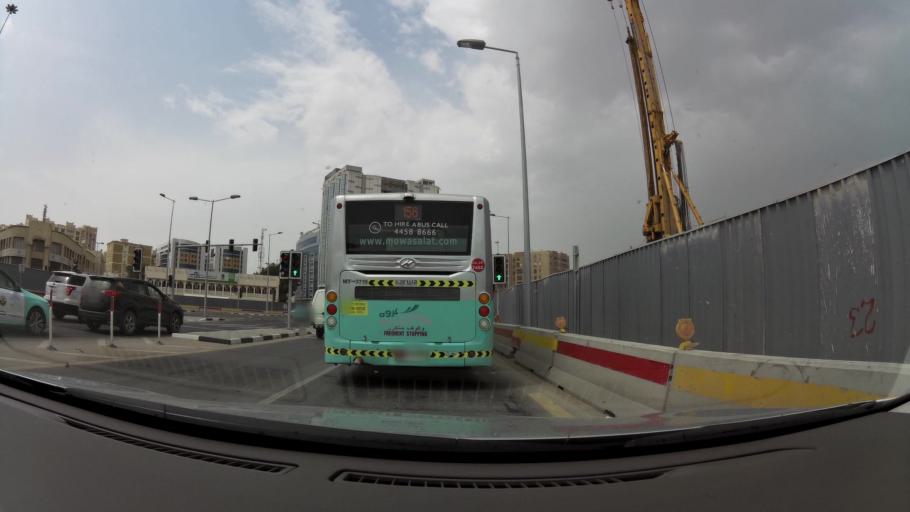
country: QA
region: Baladiyat ad Dawhah
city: Doha
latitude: 25.2821
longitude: 51.5250
